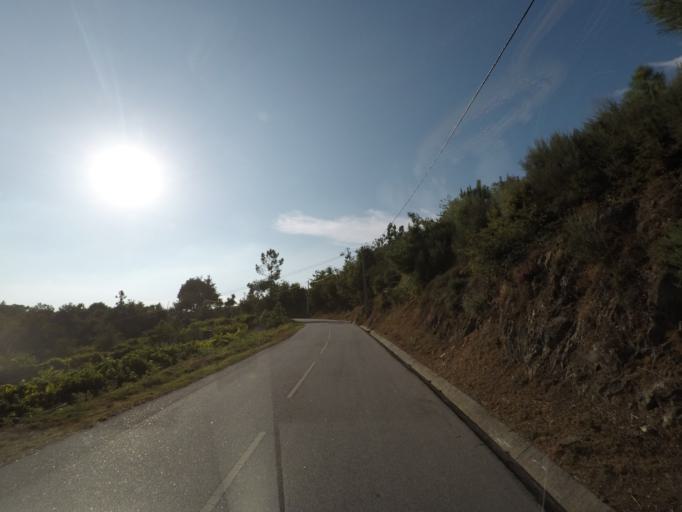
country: PT
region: Vila Real
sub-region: Mesao Frio
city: Mesao Frio
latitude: 41.1637
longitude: -7.9170
